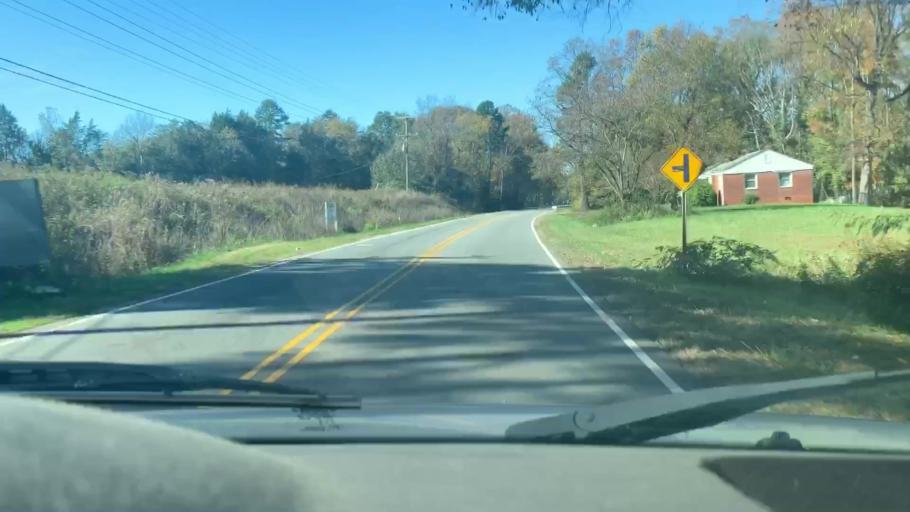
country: US
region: North Carolina
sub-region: Mecklenburg County
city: Huntersville
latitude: 35.4267
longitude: -80.9198
